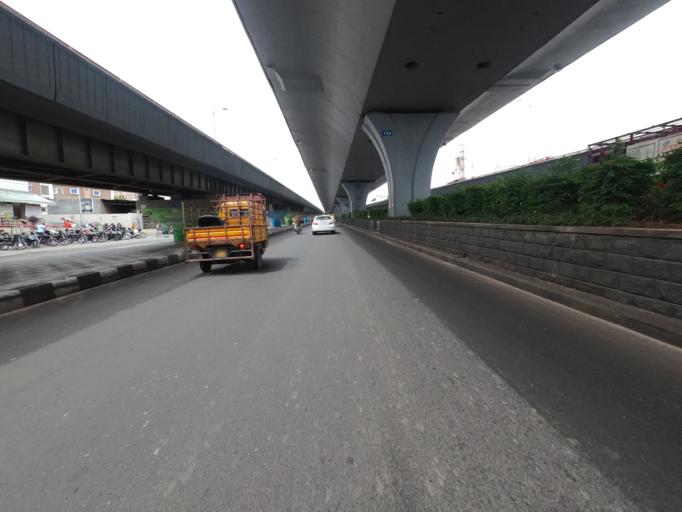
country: IN
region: Telangana
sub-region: Hyderabad
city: Hyderabad
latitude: 17.3509
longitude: 78.4175
